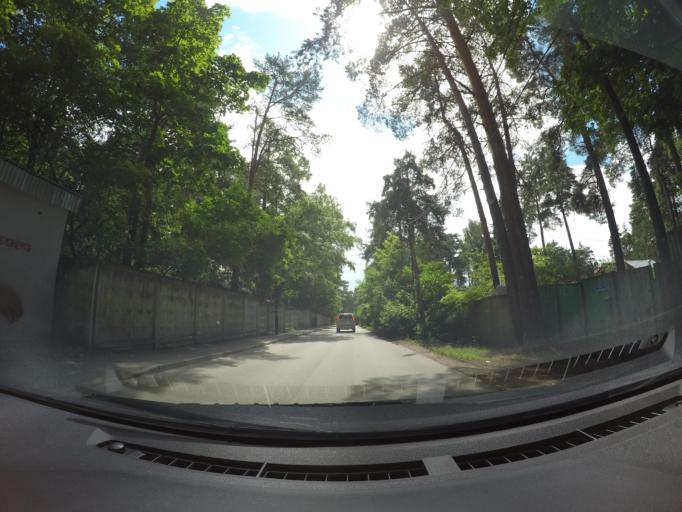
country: RU
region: Moskovskaya
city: Malakhovka
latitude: 55.6437
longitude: 38.0403
